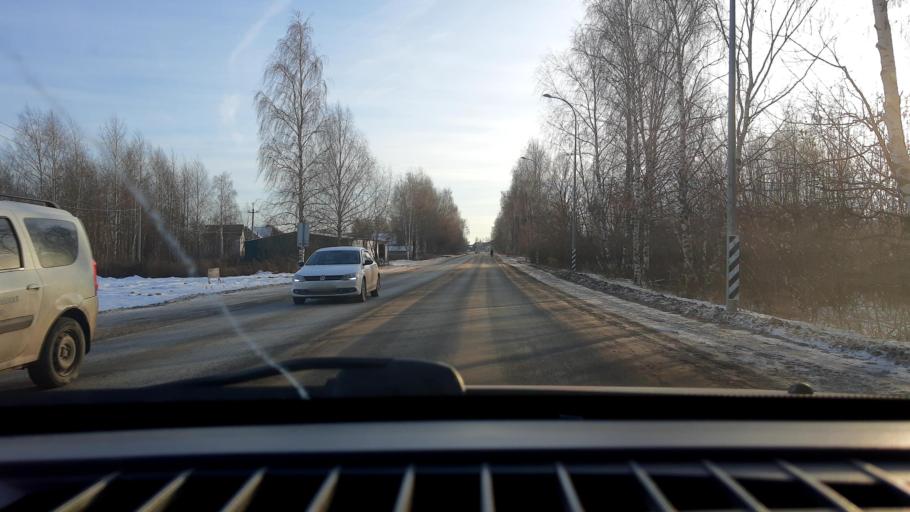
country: RU
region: Nizjnij Novgorod
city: Bor
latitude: 56.3818
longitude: 44.0374
